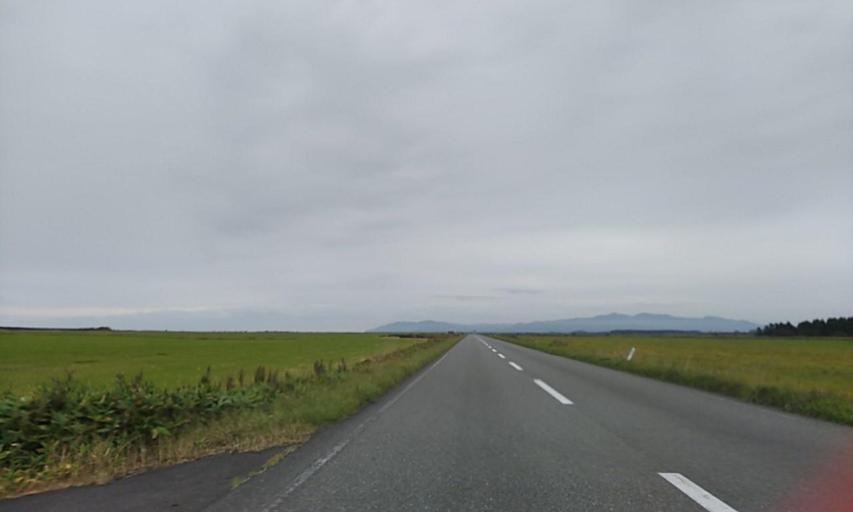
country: JP
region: Hokkaido
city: Makubetsu
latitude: 45.2133
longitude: 142.2868
